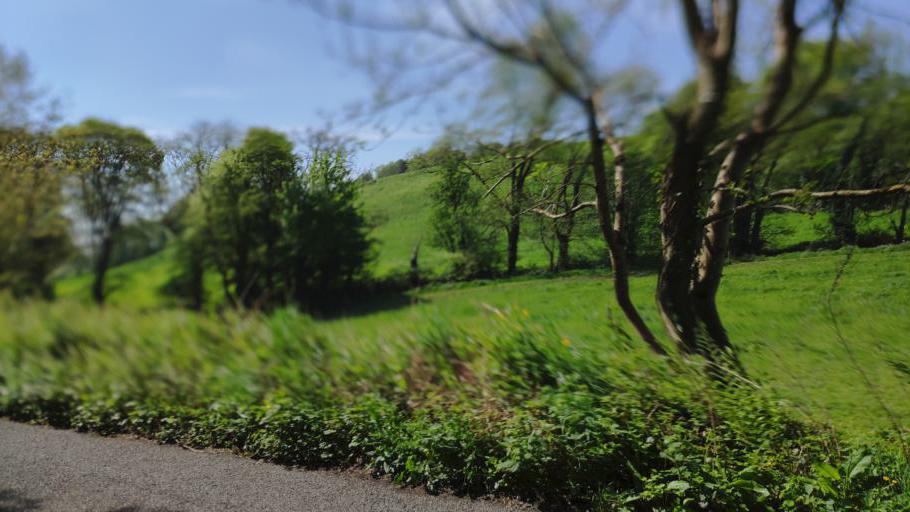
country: IE
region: Munster
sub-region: County Cork
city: Blarney
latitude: 51.9692
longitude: -8.5784
